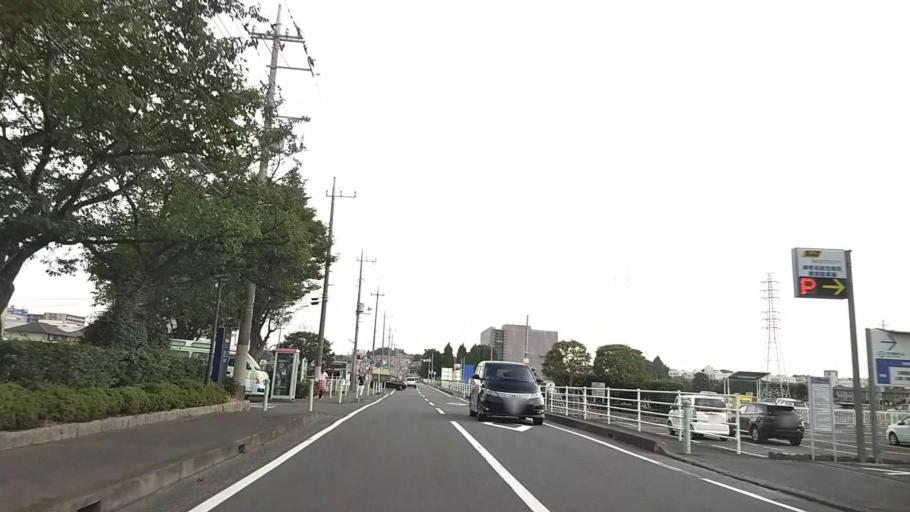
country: JP
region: Kanagawa
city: Atsugi
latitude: 35.4468
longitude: 139.3857
